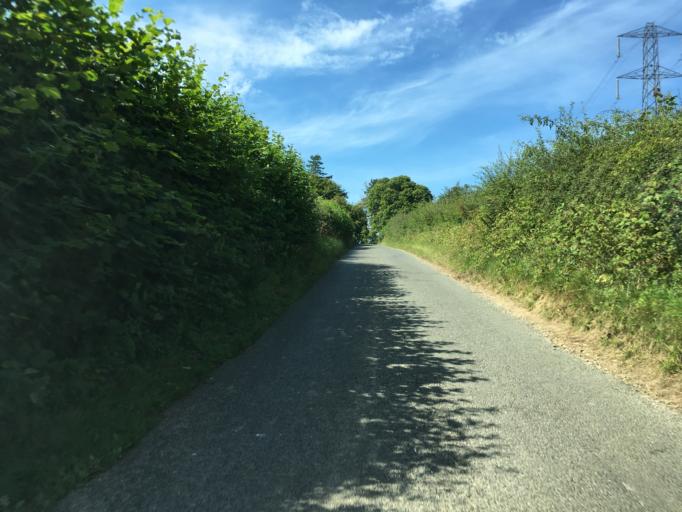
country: GB
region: England
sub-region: Hampshire
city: Highclere
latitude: 51.2898
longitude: -1.3689
